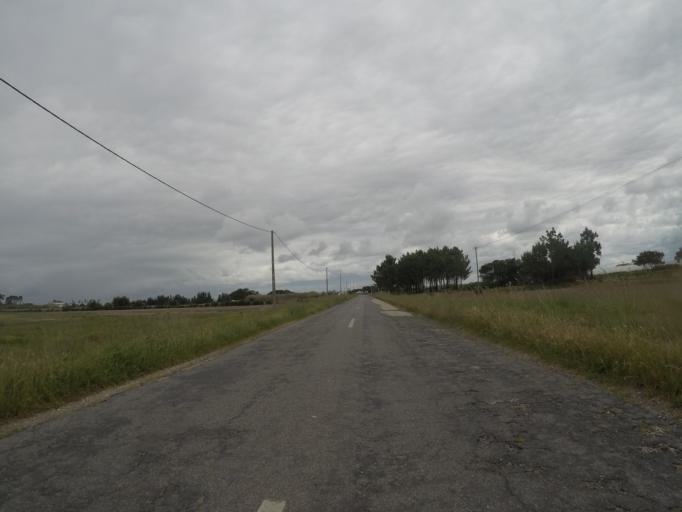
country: PT
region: Beja
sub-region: Odemira
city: Vila Nova de Milfontes
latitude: 37.6120
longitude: -8.7927
